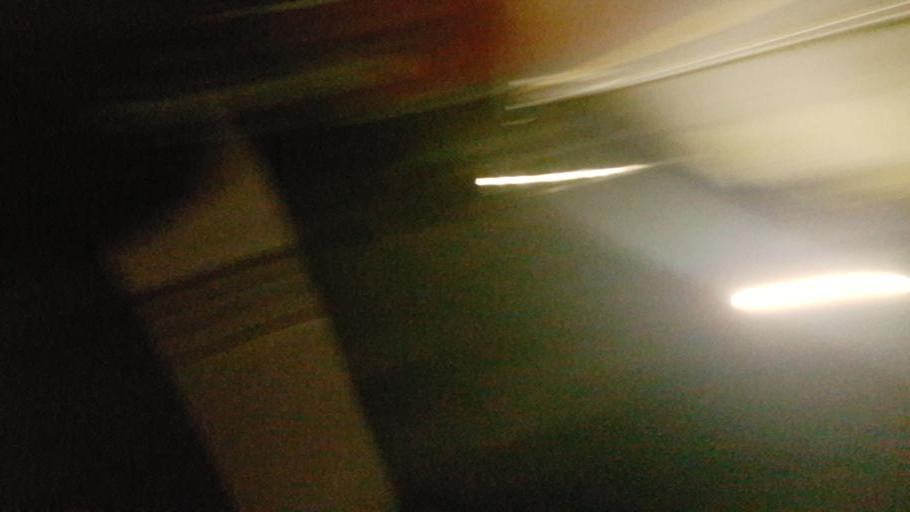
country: TW
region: Taiwan
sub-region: Hsinchu
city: Hsinchu
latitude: 24.7469
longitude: 120.9636
